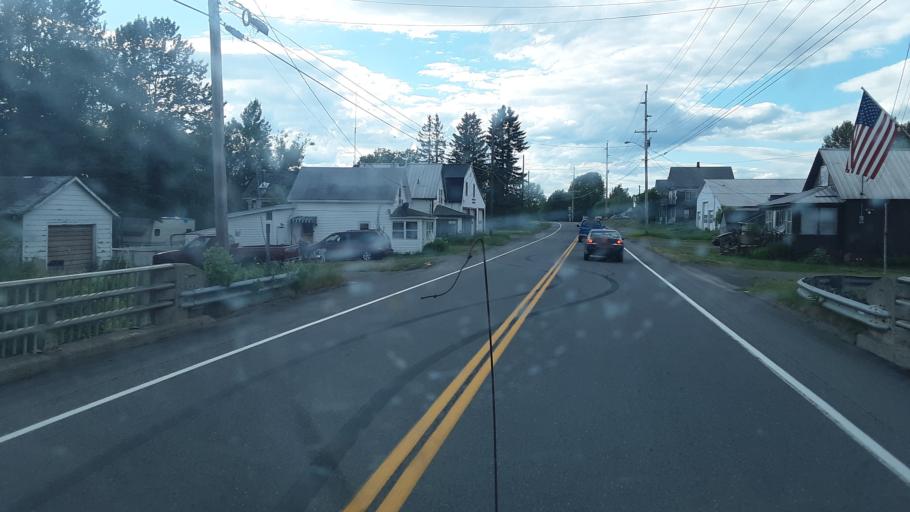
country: US
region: Maine
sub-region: Penobscot County
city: Patten
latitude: 45.8975
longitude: -68.4270
